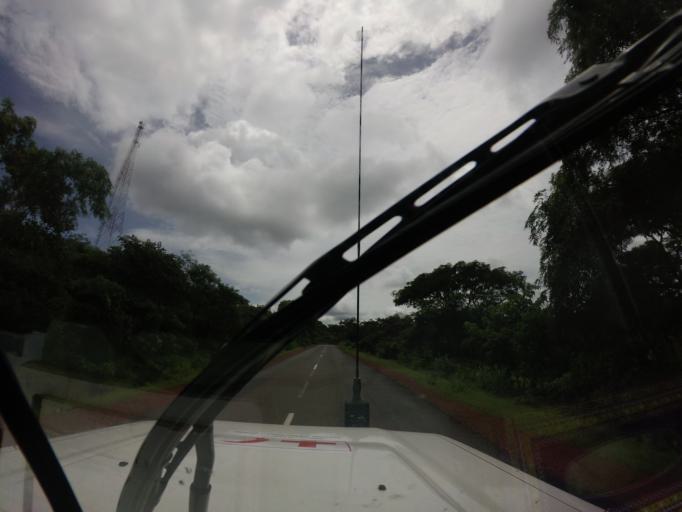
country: GN
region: Faranah
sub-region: Faranah Prefecture
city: Faranah
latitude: 10.0345
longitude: -10.9827
